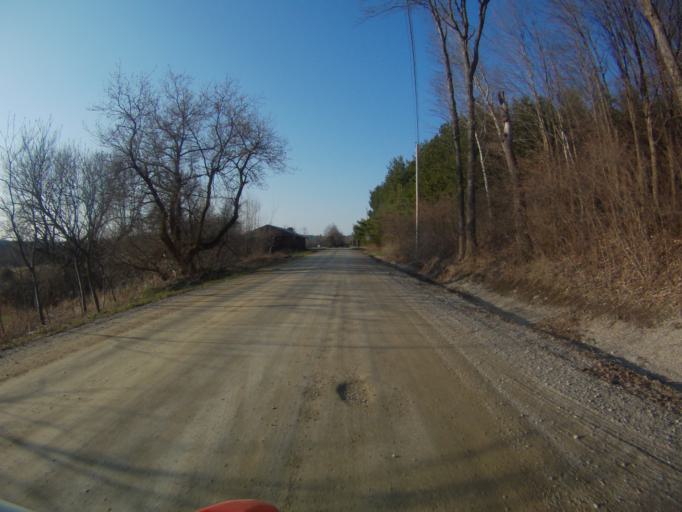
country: US
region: Vermont
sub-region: Addison County
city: Bristol
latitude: 44.1073
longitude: -73.0890
